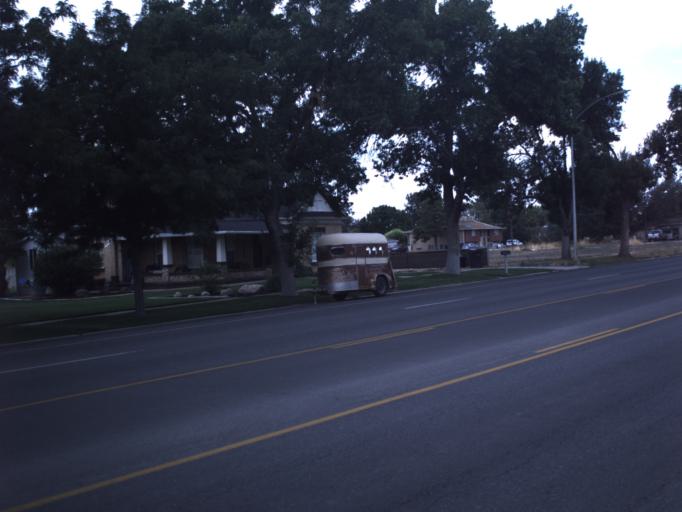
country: US
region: Utah
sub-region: Juab County
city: Nephi
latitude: 39.7001
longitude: -111.8360
